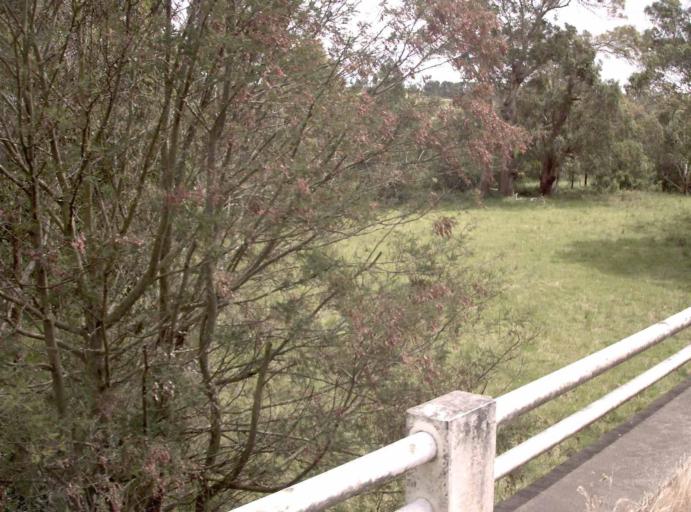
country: AU
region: Victoria
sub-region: Latrobe
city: Moe
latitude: -38.0886
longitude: 146.1599
